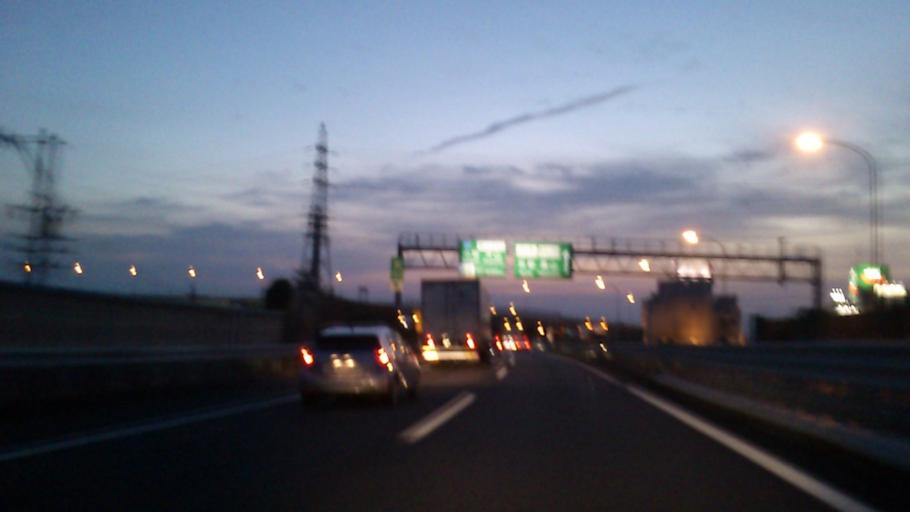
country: JP
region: Aichi
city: Komaki
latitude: 35.3024
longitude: 136.9142
